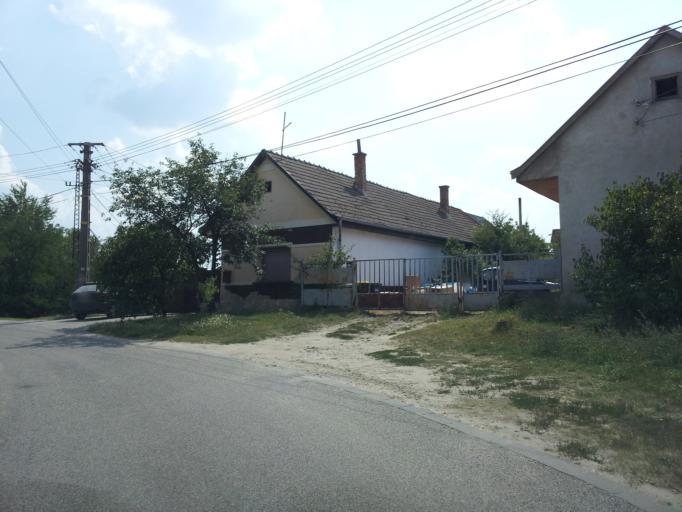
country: HU
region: Pest
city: Taksony
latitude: 47.3314
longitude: 19.0598
